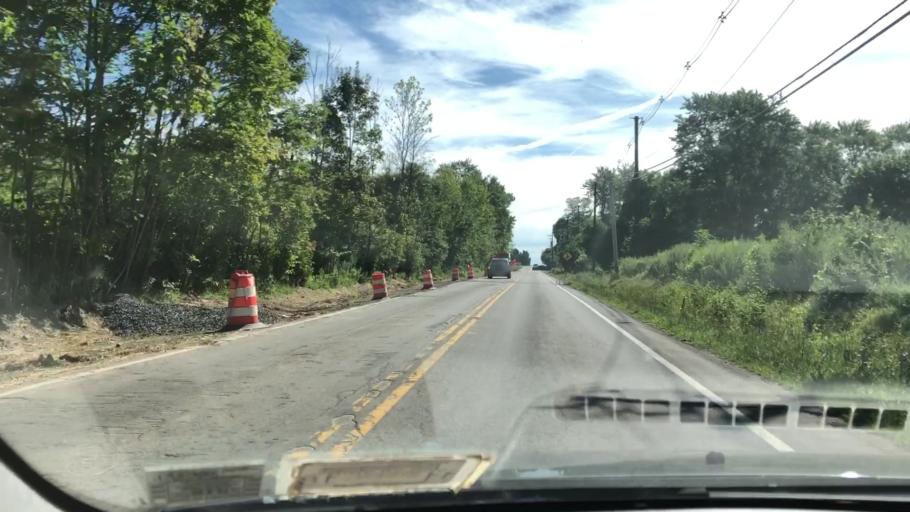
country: US
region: New York
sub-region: Monroe County
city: Fairport
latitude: 43.1086
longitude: -77.4007
